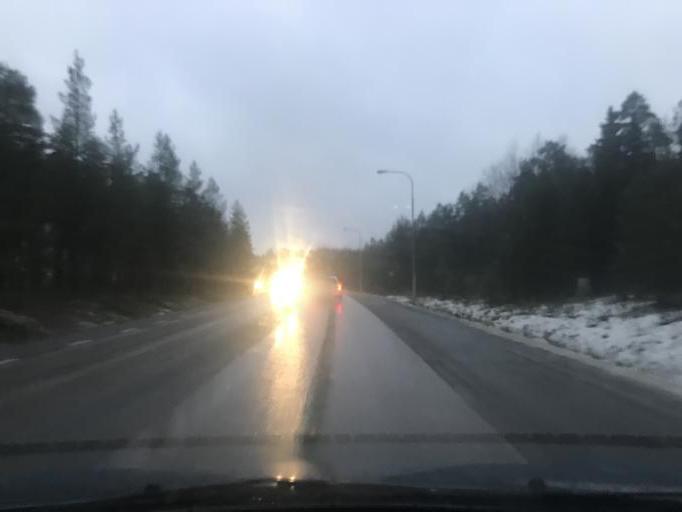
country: SE
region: Norrbotten
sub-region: Lulea Kommun
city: Gammelstad
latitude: 65.6227
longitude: 22.0353
